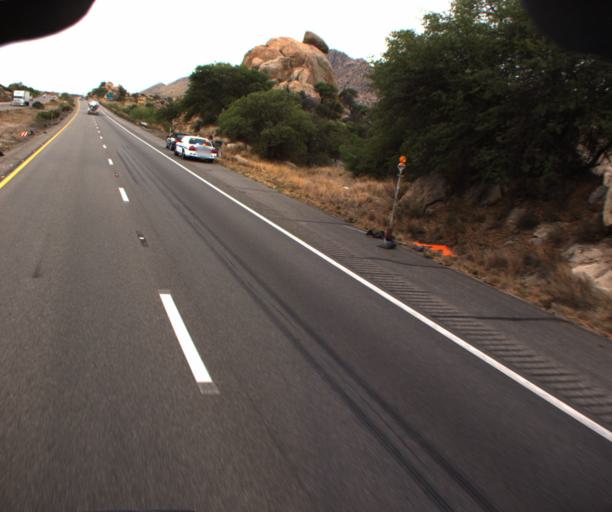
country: US
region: Arizona
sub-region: Cochise County
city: Saint David
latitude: 32.0505
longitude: -110.0862
